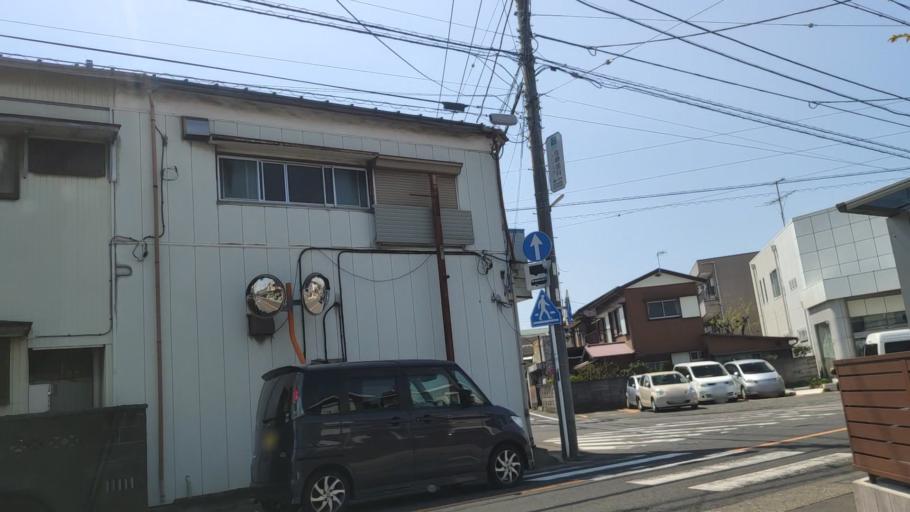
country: JP
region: Kanagawa
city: Hiratsuka
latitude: 35.3377
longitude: 139.3315
